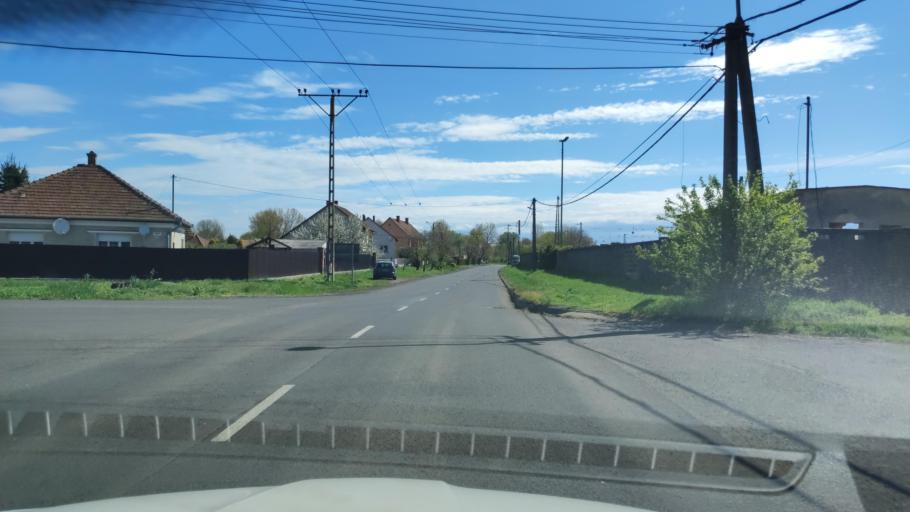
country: HU
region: Pest
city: Abony
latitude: 47.1738
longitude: 20.0165
